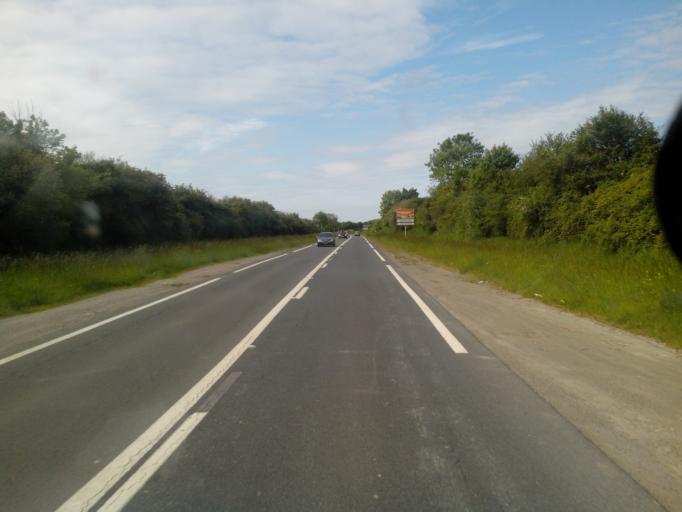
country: FR
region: Lower Normandy
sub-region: Departement du Calvados
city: Dives-sur-Mer
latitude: 49.2611
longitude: -0.1040
